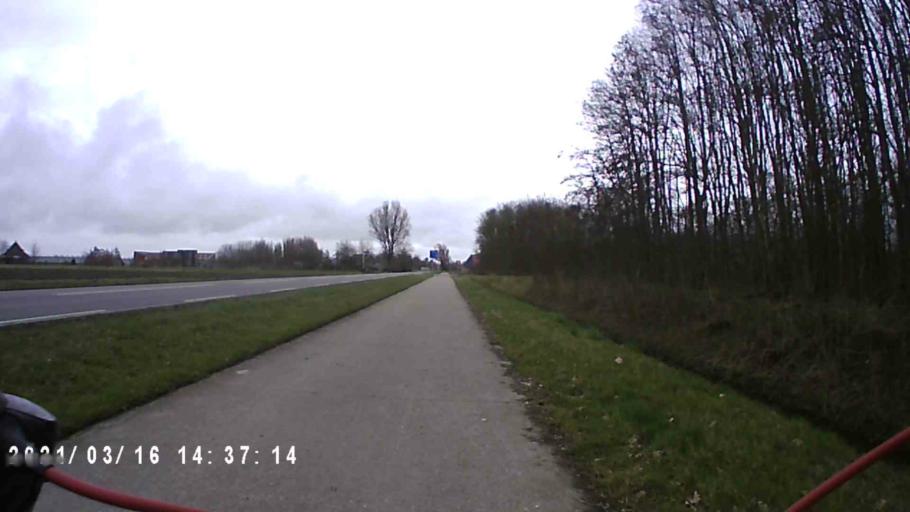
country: NL
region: Friesland
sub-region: Gemeente Harlingen
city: Harlingen
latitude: 53.1446
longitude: 5.4257
